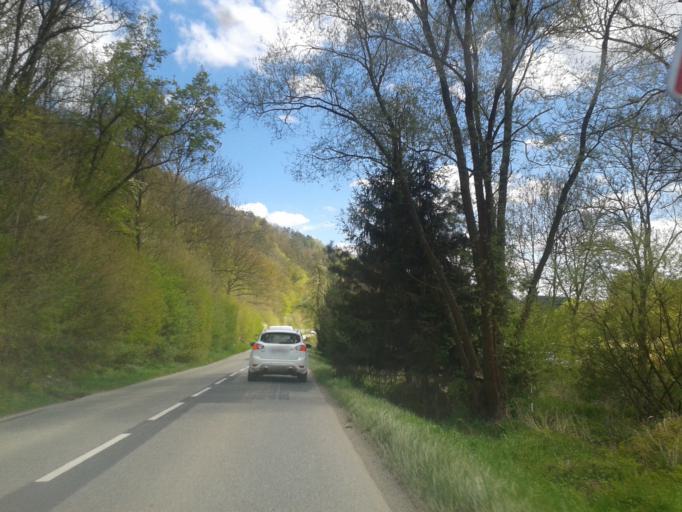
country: CZ
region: Central Bohemia
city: Hyskov
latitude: 49.9899
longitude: 14.0622
